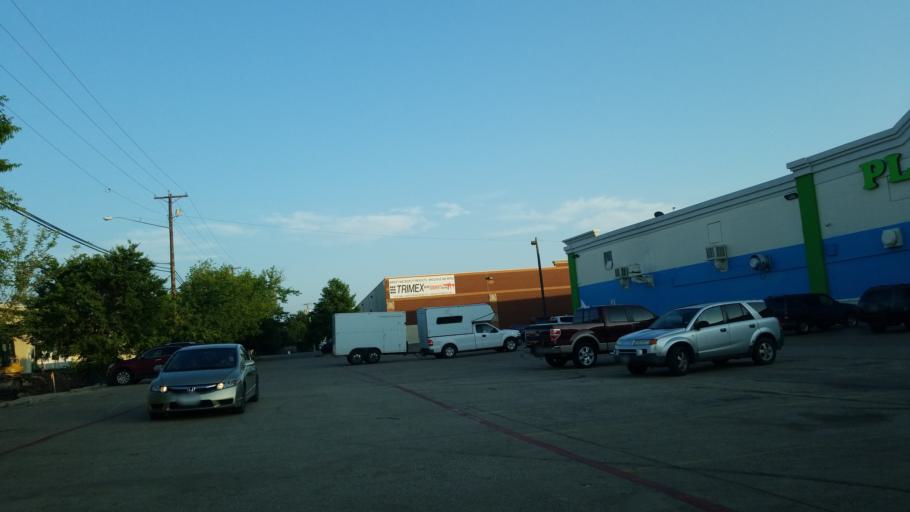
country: US
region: Texas
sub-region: Dallas County
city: Farmers Branch
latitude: 32.8898
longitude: -96.8868
